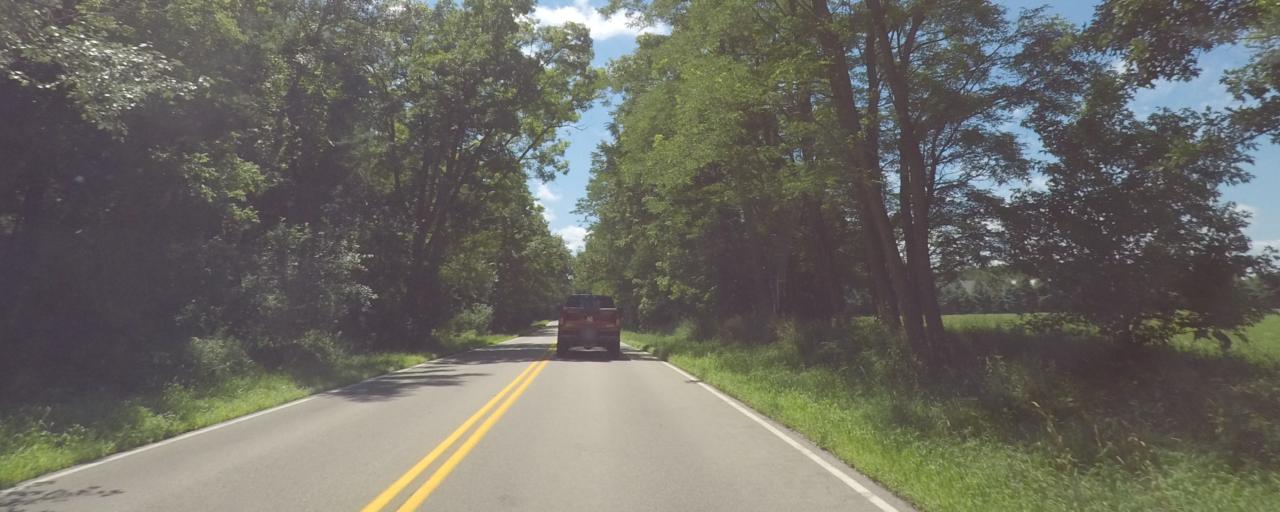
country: US
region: Wisconsin
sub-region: Waukesha County
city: Eagle
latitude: 42.9303
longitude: -88.5123
